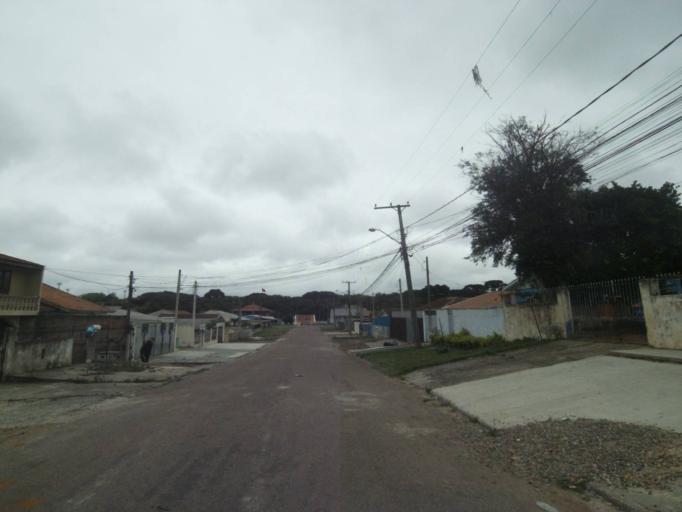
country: BR
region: Parana
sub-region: Sao Jose Dos Pinhais
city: Sao Jose dos Pinhais
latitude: -25.5450
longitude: -49.2778
